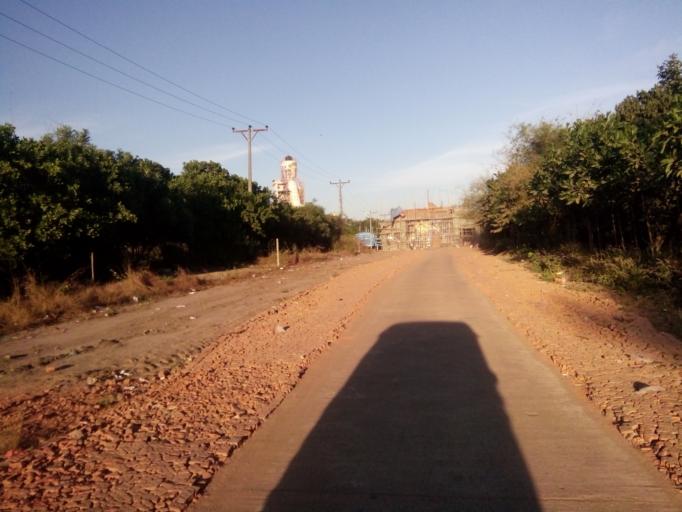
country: MM
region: Bago
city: Thanatpin
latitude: 17.2721
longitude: 96.2334
